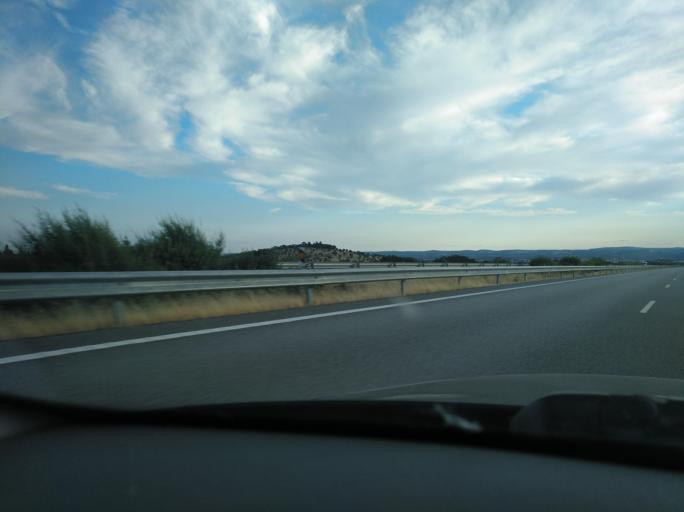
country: PT
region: Portalegre
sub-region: Elvas
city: Elvas
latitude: 38.8741
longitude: -7.2766
